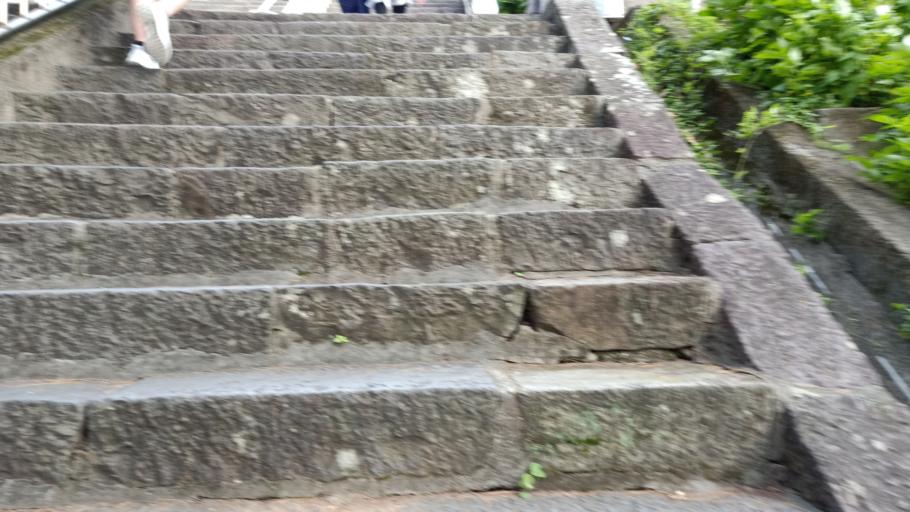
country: TW
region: Taipei
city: Taipei
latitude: 25.1734
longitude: 121.4475
